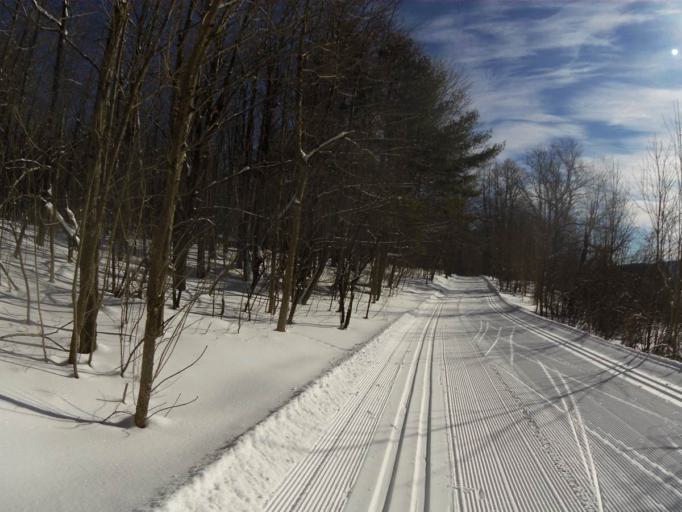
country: CA
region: Quebec
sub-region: Outaouais
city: Wakefield
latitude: 45.5882
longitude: -75.9781
